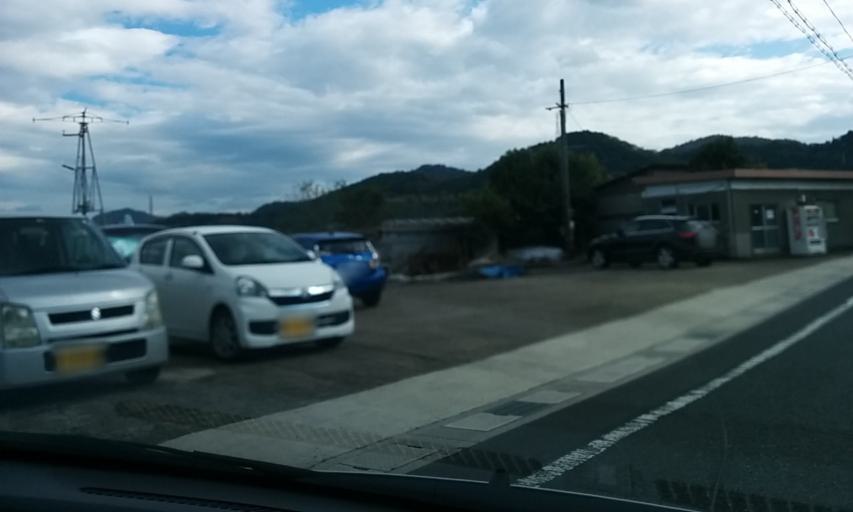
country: JP
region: Kyoto
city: Fukuchiyama
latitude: 35.3037
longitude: 135.1772
